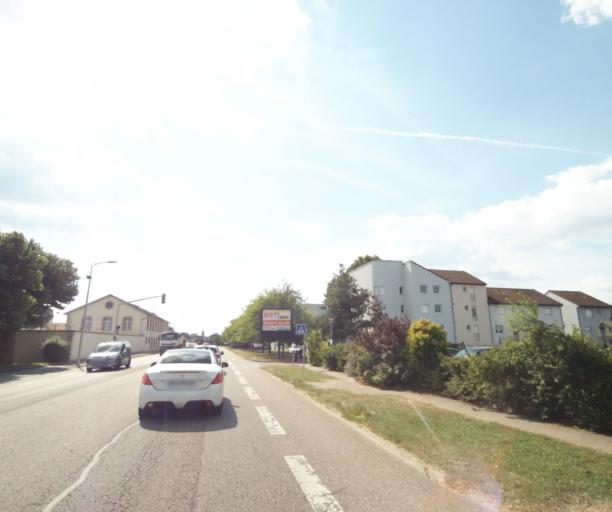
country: FR
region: Lorraine
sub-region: Departement de Meurthe-et-Moselle
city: Chanteheux
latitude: 48.5920
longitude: 6.5153
